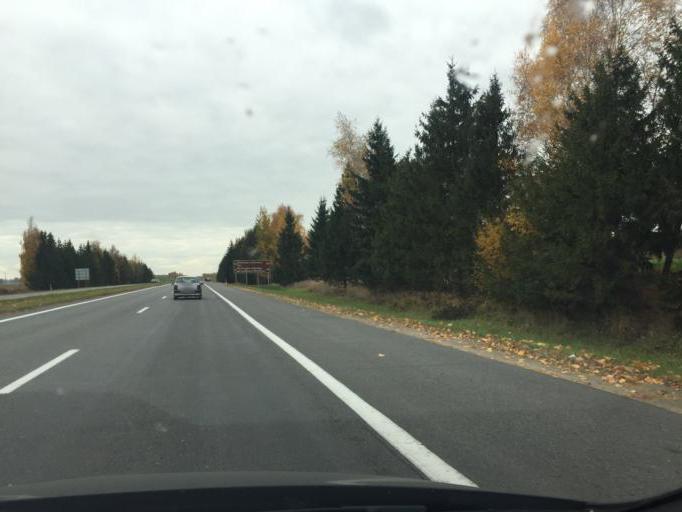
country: BY
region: Minsk
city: Samakhvalavichy
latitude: 53.7219
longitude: 27.4995
